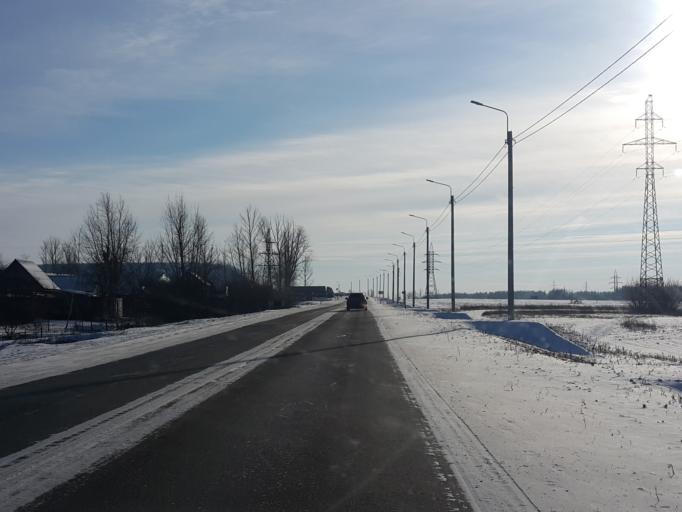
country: RU
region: Tambov
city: Znamenka
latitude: 52.4297
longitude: 41.5003
